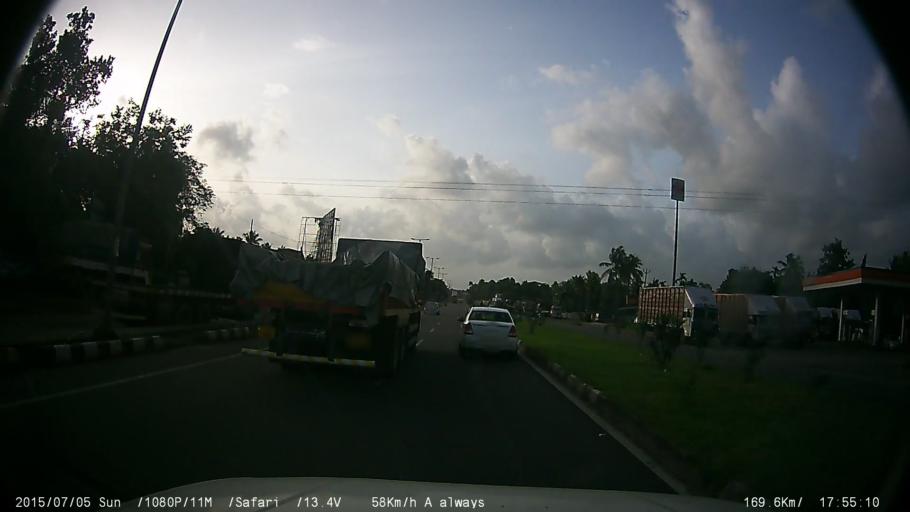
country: IN
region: Kerala
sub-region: Ernakulam
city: Angamali
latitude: 10.2492
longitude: 76.3689
